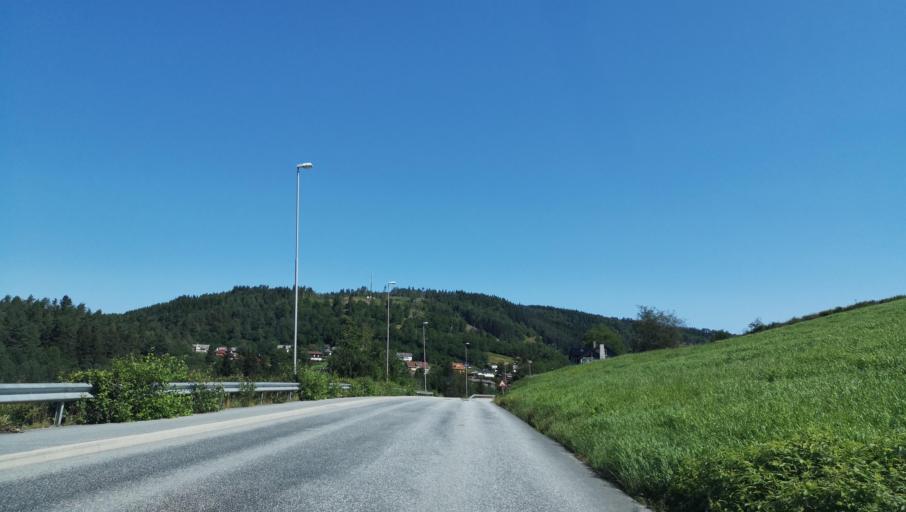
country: NO
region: Hordaland
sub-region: Voss
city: Voss
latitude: 60.6328
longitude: 6.4478
